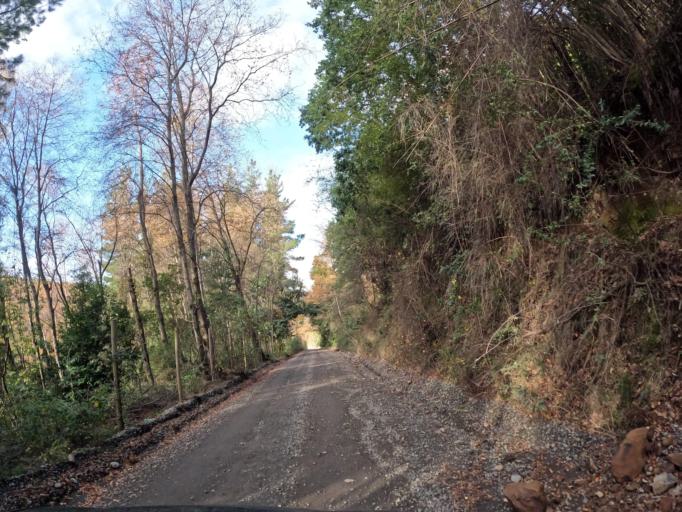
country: CL
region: Biobio
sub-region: Provincia de Nuble
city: Coihueco
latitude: -36.7993
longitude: -71.7291
